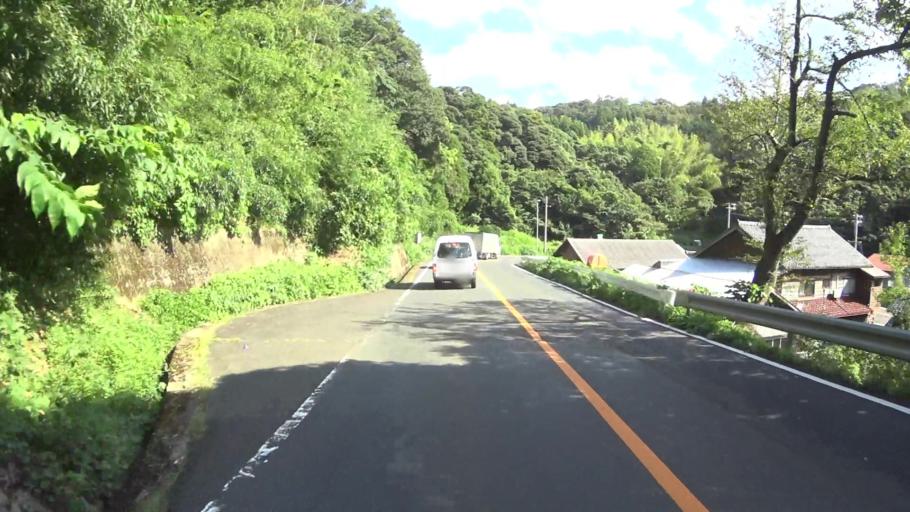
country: JP
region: Kyoto
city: Miyazu
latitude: 35.7497
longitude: 135.1675
